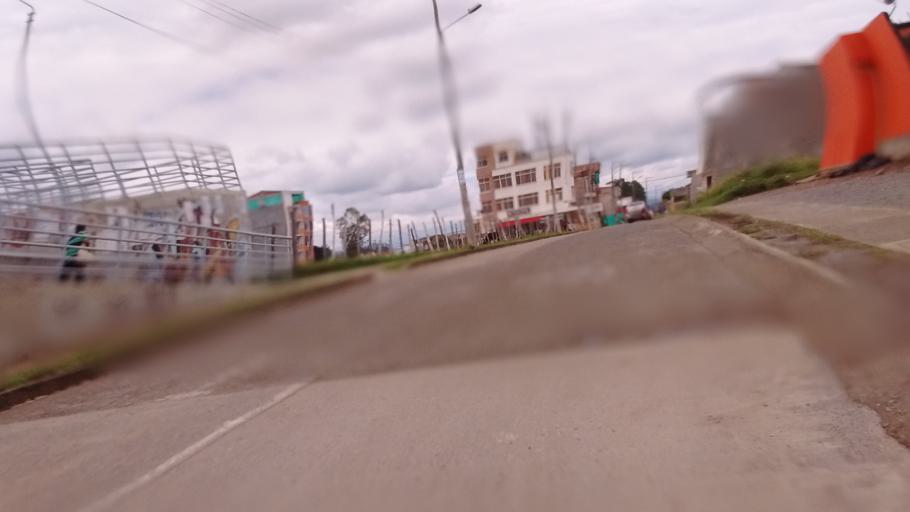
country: CO
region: Cauca
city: Popayan
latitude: 2.4787
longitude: -76.5762
